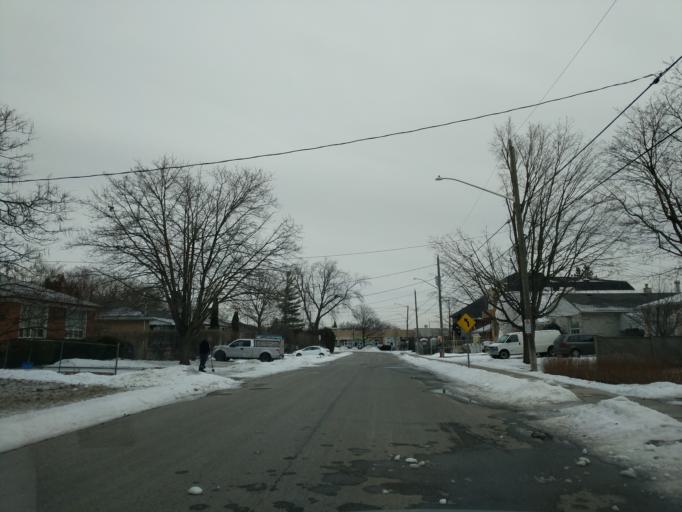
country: CA
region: Ontario
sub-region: York
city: Richmond Hill
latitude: 43.8769
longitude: -79.4180
